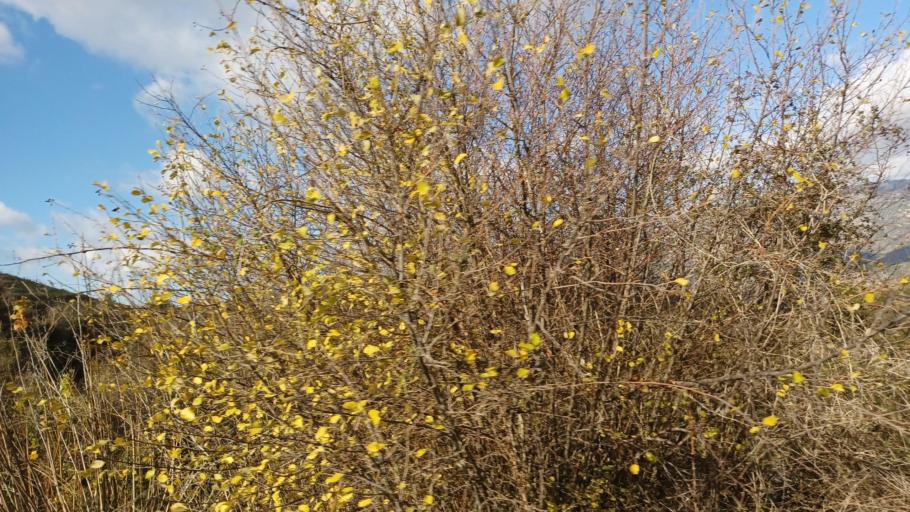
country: CY
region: Limassol
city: Pachna
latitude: 34.8552
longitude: 32.6907
